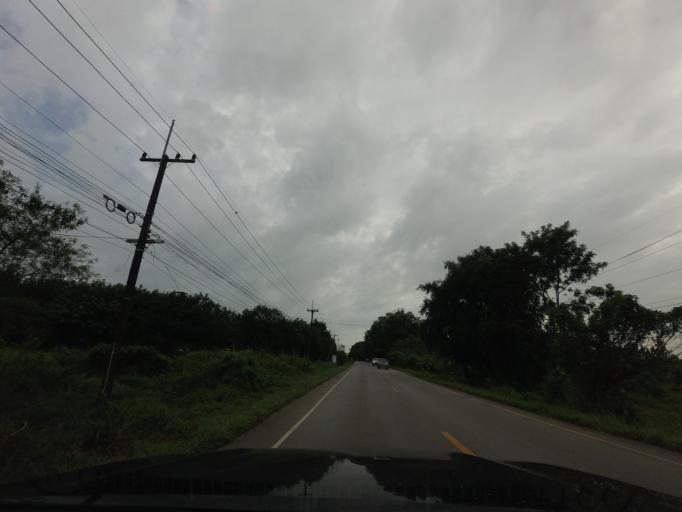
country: TH
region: Changwat Udon Thani
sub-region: Amphoe Ban Phue
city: Ban Phue
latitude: 17.7211
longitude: 102.3929
